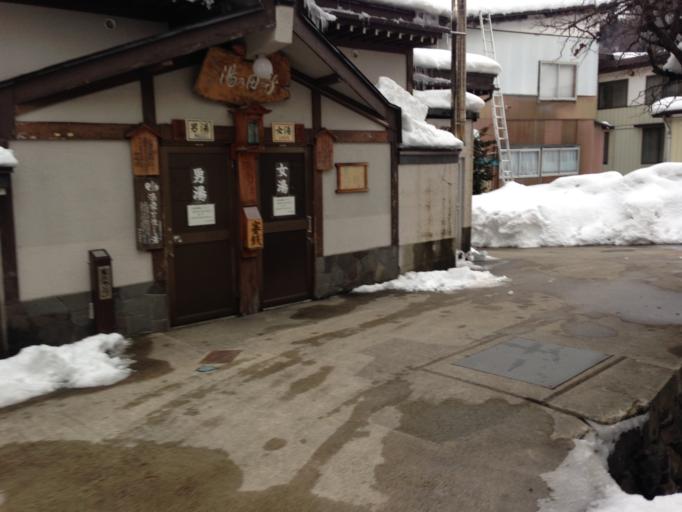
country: JP
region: Nagano
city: Iiyama
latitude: 36.9207
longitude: 138.4455
